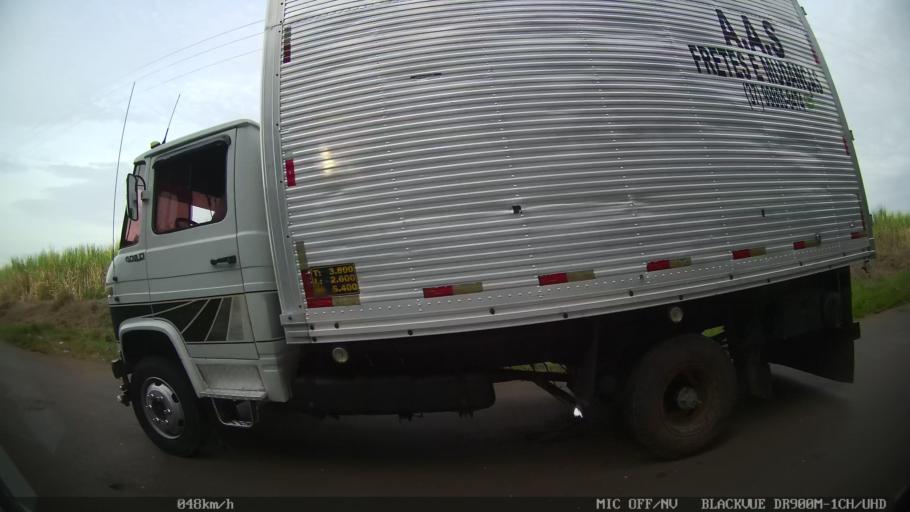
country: BR
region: Sao Paulo
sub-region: Piracicaba
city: Piracicaba
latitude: -22.7120
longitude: -47.5802
